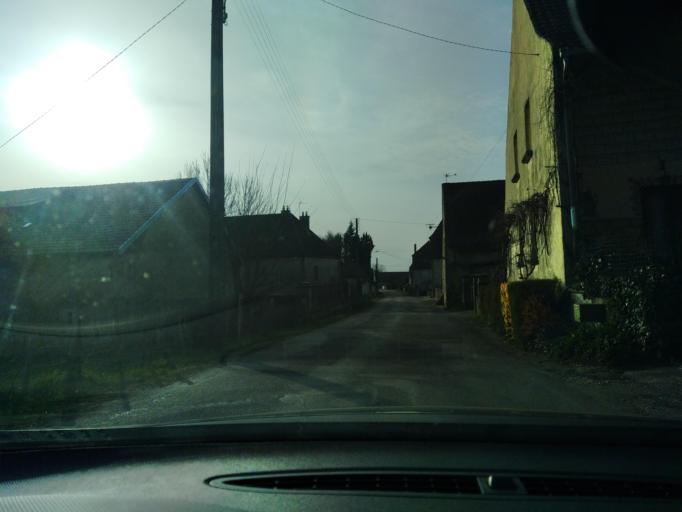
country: FR
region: Franche-Comte
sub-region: Departement du Jura
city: Chaussin
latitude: 46.9886
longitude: 5.4579
